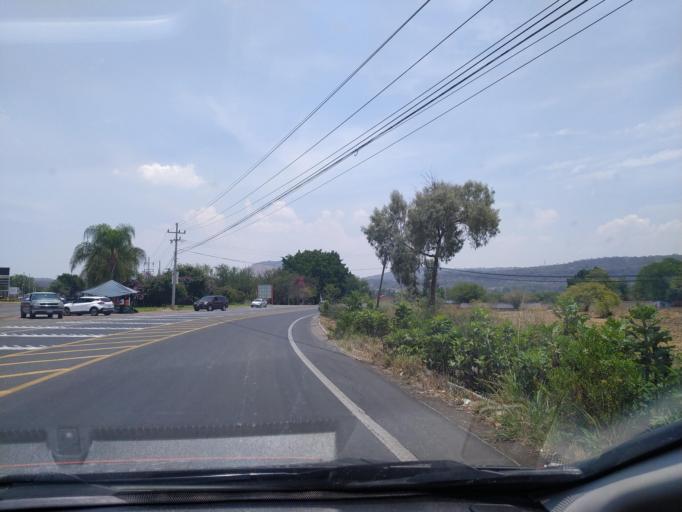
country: MX
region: Jalisco
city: Bellavista
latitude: 20.4118
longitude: -103.5935
